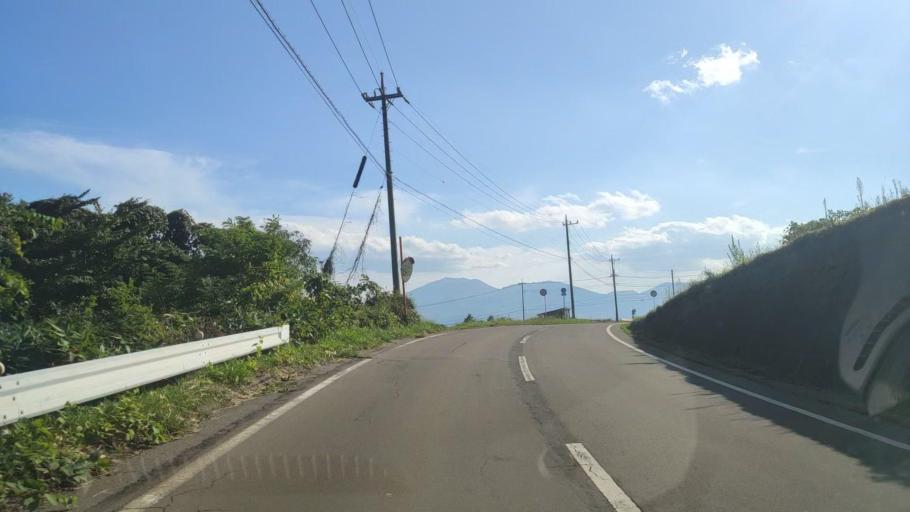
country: JP
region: Nagano
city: Suzaka
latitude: 36.5790
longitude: 138.5648
